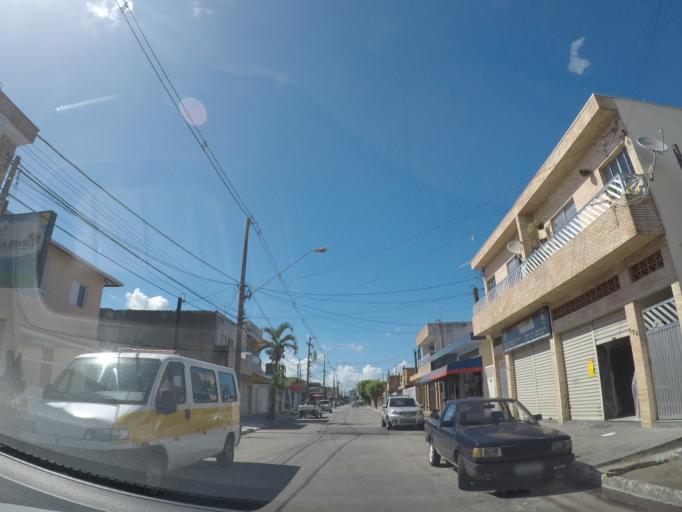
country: BR
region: Sao Paulo
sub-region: Praia Grande
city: Praia Grande
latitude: -24.0274
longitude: -46.5125
